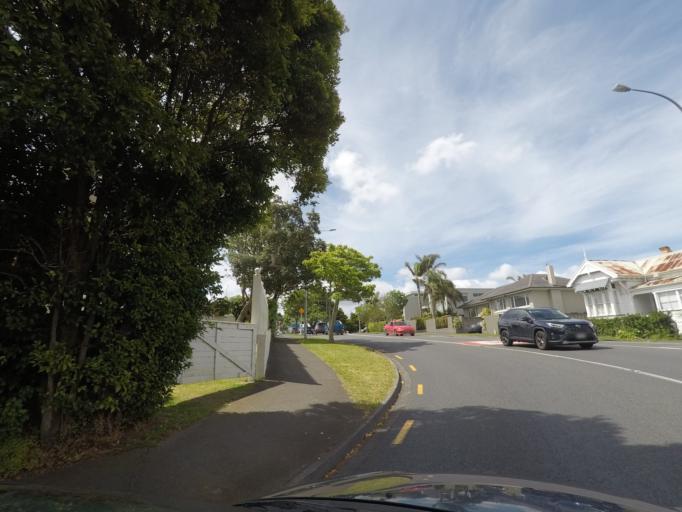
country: NZ
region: Auckland
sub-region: Auckland
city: Auckland
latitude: -36.8491
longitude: 174.7300
